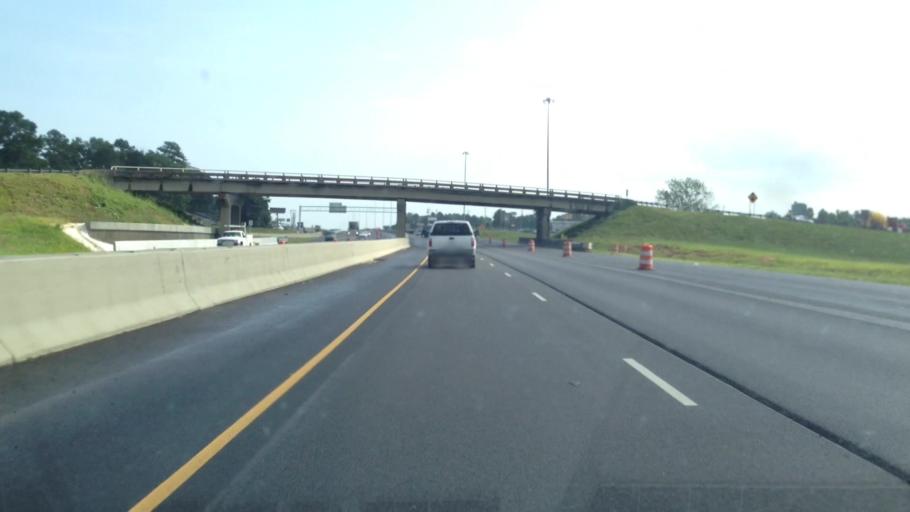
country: US
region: Mississippi
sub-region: Rankin County
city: Richland
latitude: 32.2413
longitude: -90.2156
